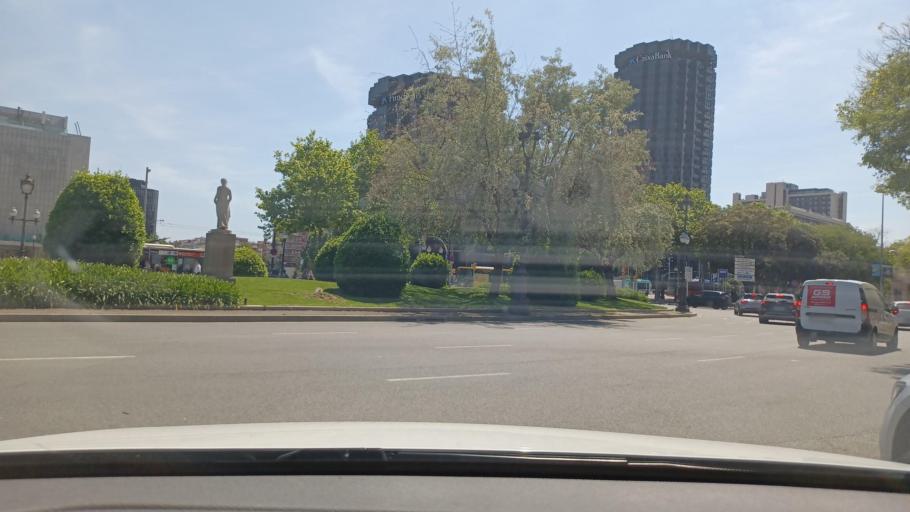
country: ES
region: Catalonia
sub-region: Provincia de Barcelona
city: les Corts
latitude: 41.3890
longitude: 2.1275
